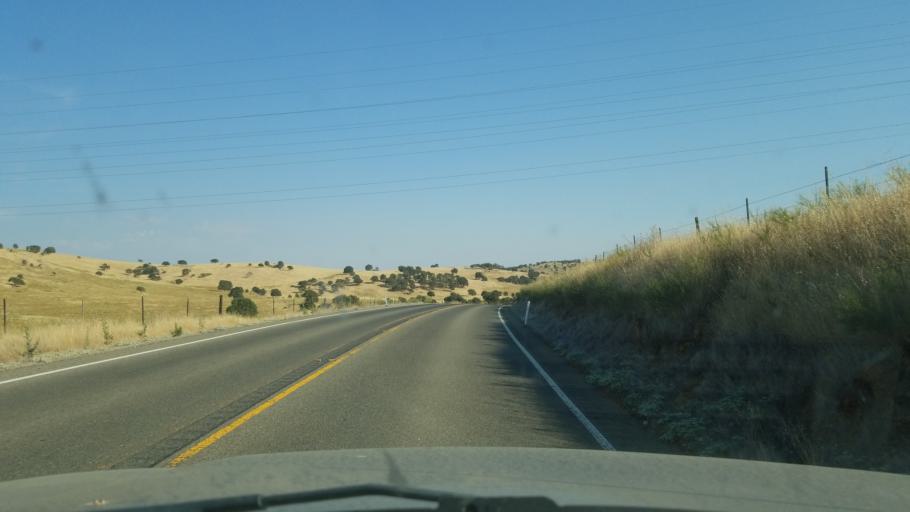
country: US
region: California
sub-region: Tuolumne County
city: Jamestown
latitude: 37.7883
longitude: -120.4643
